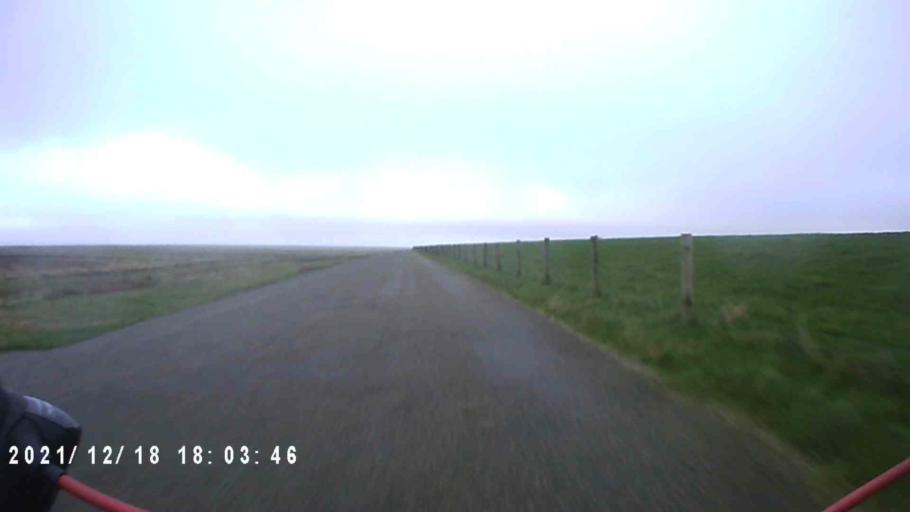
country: NL
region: Friesland
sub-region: Gemeente Dongeradeel
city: Holwerd
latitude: 53.3816
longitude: 5.8990
